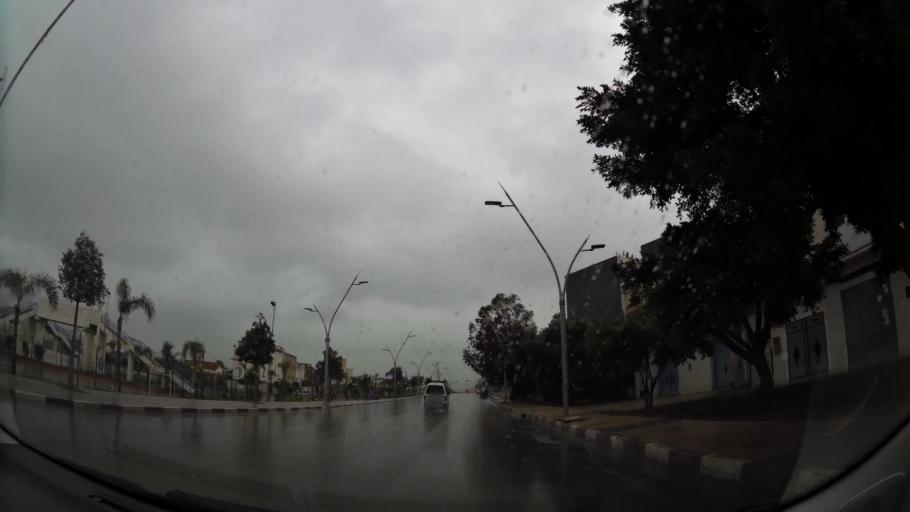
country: MA
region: Oriental
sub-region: Nador
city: Nador
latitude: 35.1576
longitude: -2.9742
